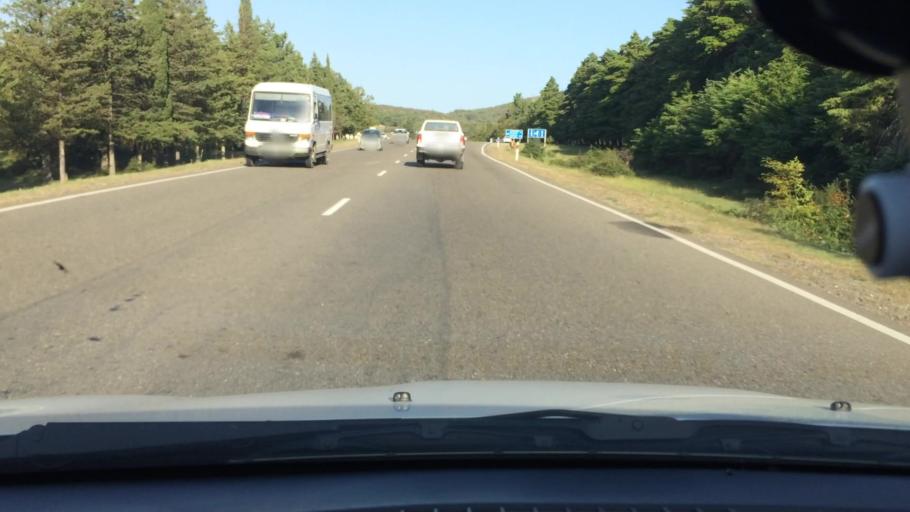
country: GE
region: Imereti
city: Kutaisi
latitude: 42.2377
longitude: 42.7688
